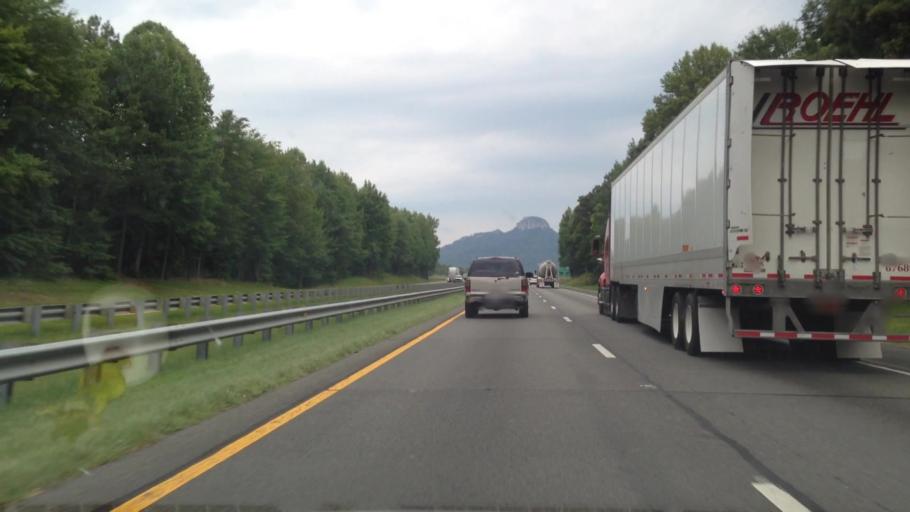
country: US
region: North Carolina
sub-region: Stokes County
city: King
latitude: 36.3134
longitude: -80.4323
